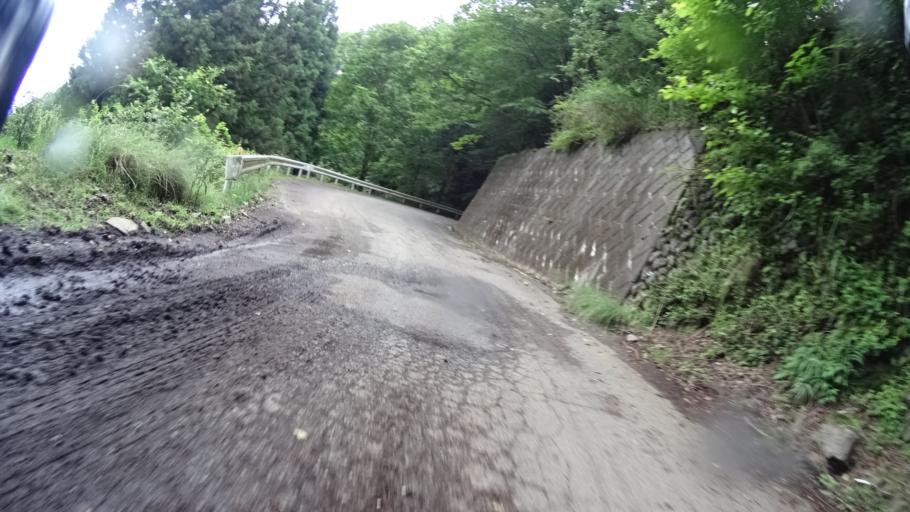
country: JP
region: Saitama
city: Chichibu
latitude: 35.8847
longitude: 139.1171
